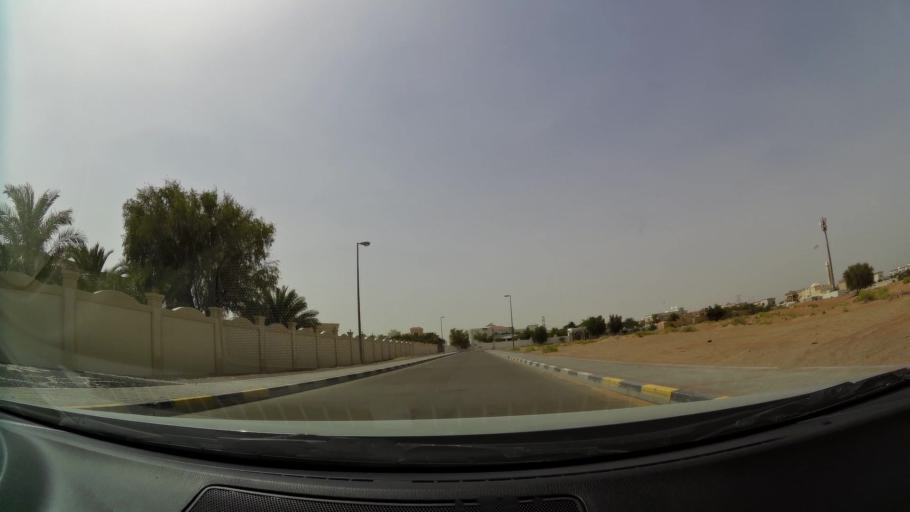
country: AE
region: Abu Dhabi
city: Al Ain
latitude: 24.1490
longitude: 55.6474
